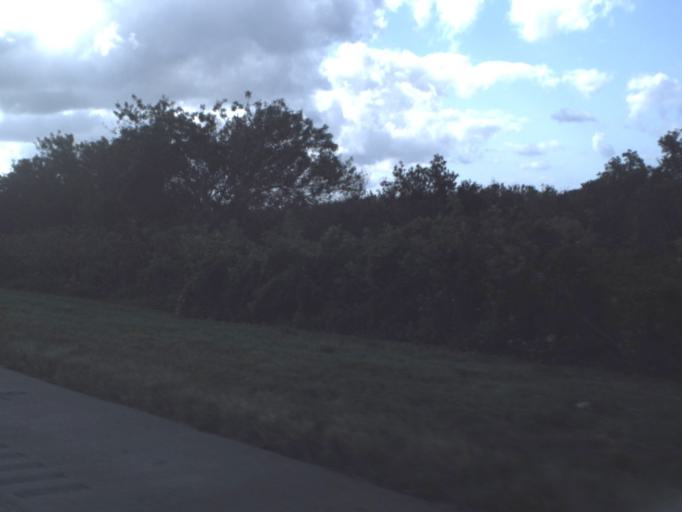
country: US
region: Florida
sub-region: Brevard County
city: Port Saint John
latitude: 28.4274
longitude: -80.8520
